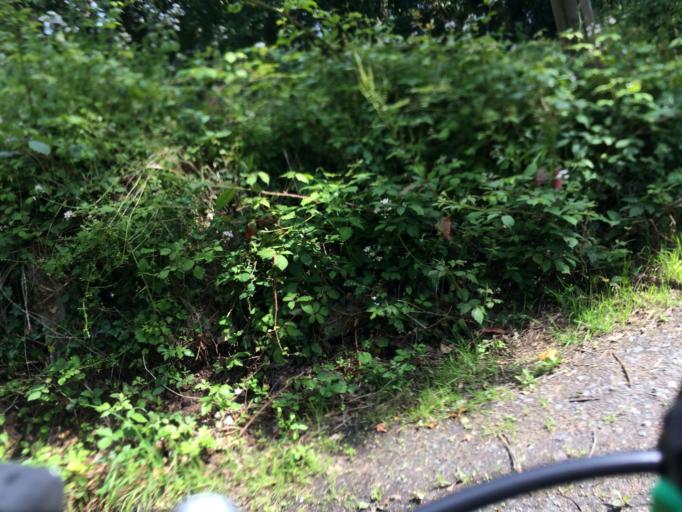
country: FR
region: Brittany
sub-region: Departement du Finistere
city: Logonna-Daoulas
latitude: 48.3153
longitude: -4.2892
